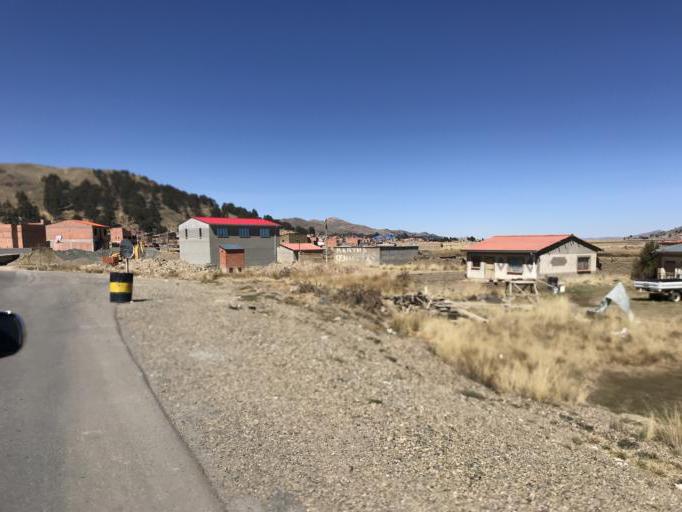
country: BO
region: La Paz
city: Huarina
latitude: -16.1896
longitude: -68.6070
